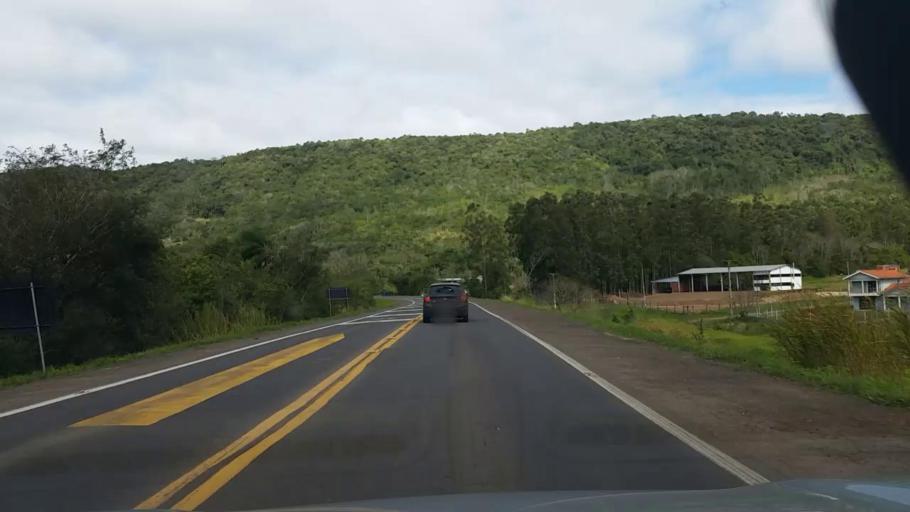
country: BR
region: Rio Grande do Sul
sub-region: Arroio Do Meio
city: Arroio do Meio
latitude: -29.3282
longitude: -52.1018
